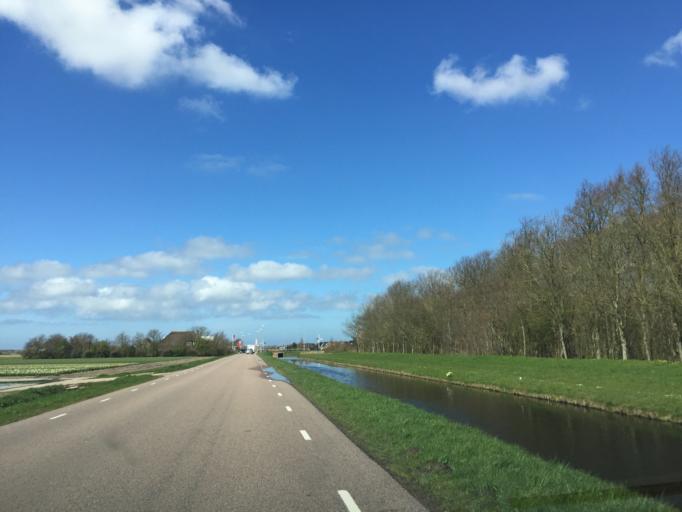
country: NL
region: North Holland
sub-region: Gemeente Den Helder
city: Den Helder
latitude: 52.8800
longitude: 4.7538
